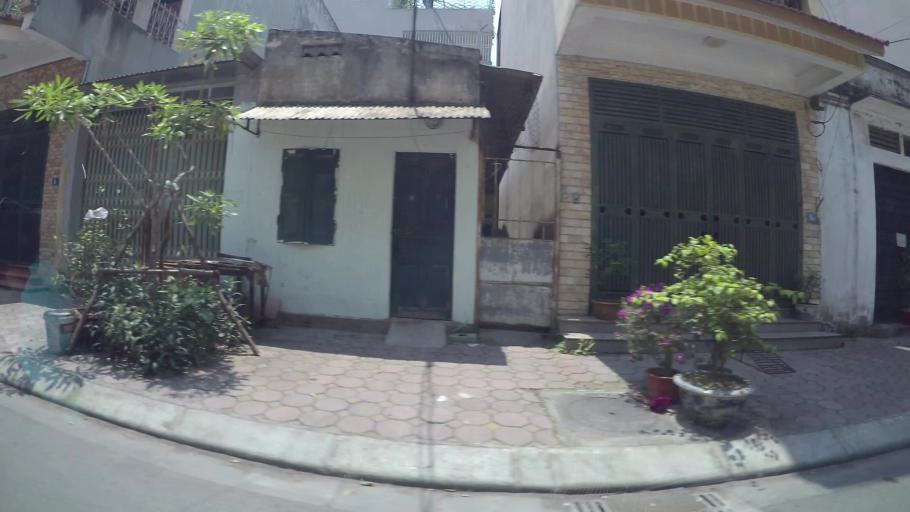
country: VN
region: Ha Noi
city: Trau Quy
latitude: 21.0347
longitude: 105.8993
